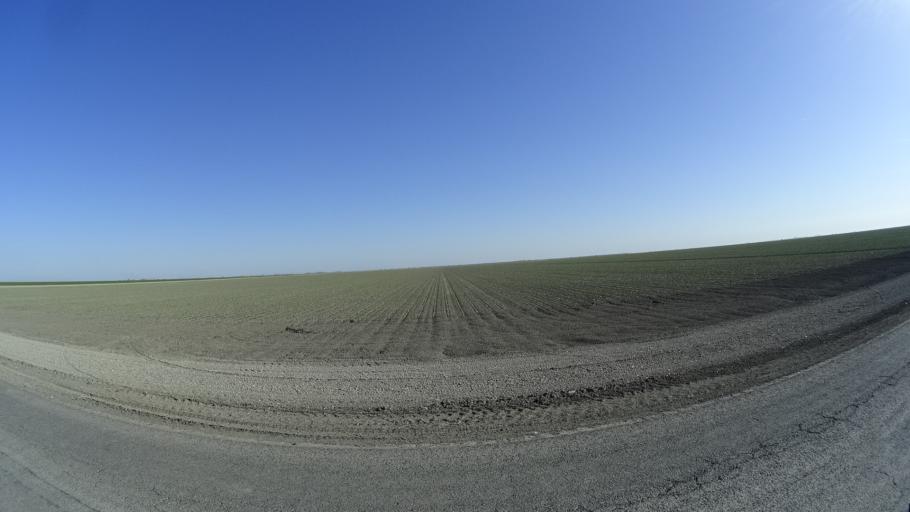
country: US
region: California
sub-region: Kings County
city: Stratford
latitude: 36.0797
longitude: -119.7315
